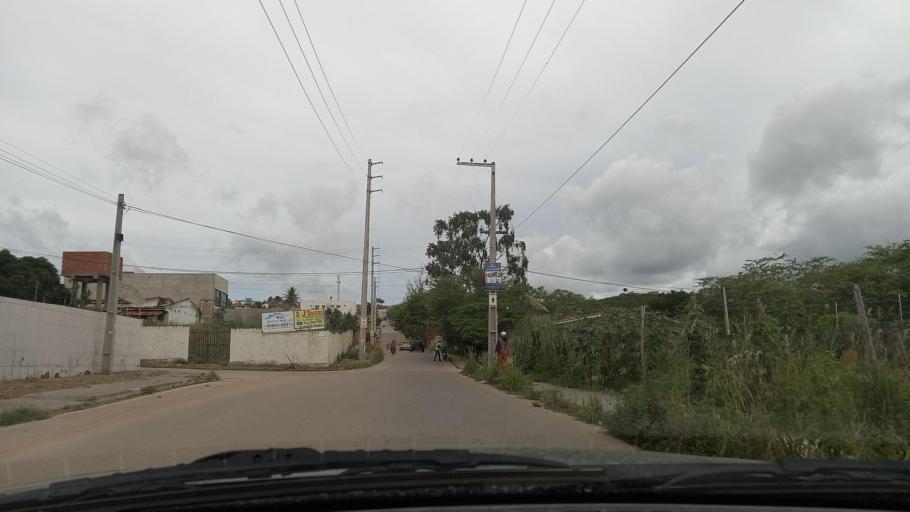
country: BR
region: Pernambuco
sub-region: Gravata
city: Gravata
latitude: -8.2062
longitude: -35.5803
